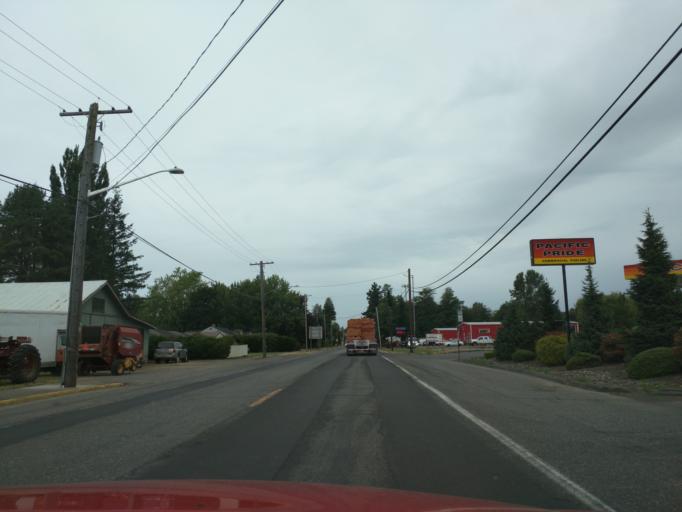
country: US
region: Washington
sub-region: Whatcom County
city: Nooksack
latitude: 48.9214
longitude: -122.3219
